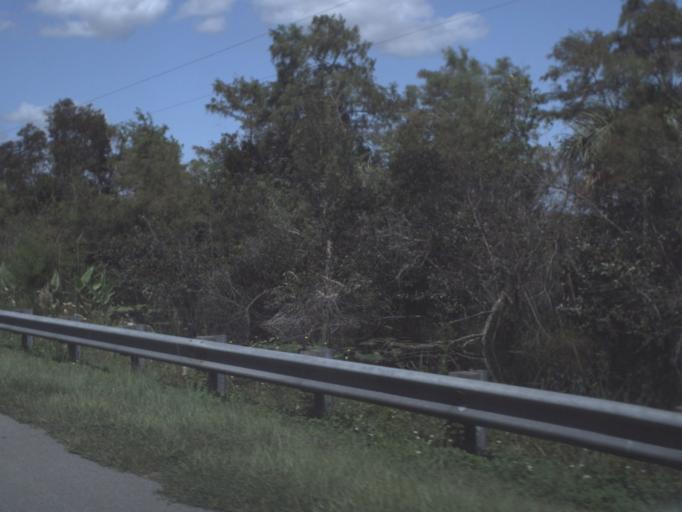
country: US
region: Florida
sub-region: Miami-Dade County
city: Kendall West
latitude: 25.8201
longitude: -80.8902
